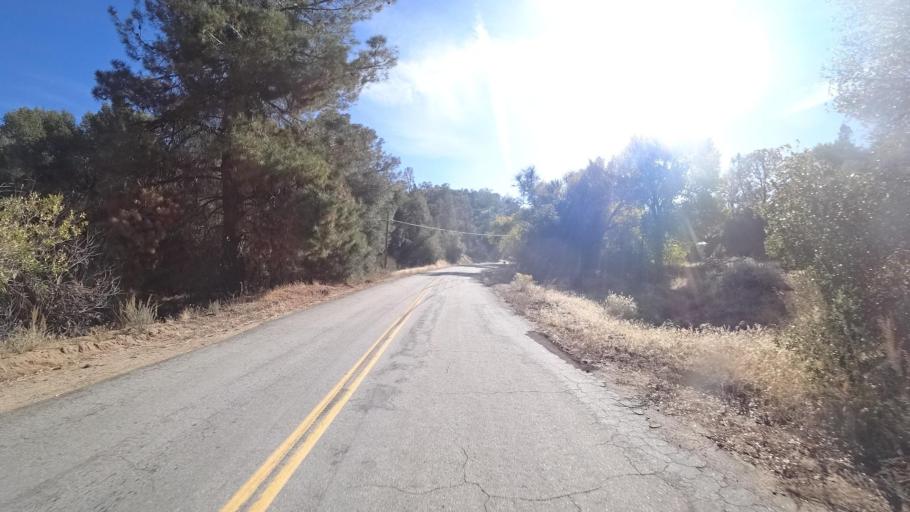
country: US
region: California
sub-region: Kern County
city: Bodfish
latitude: 35.4796
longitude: -118.5292
